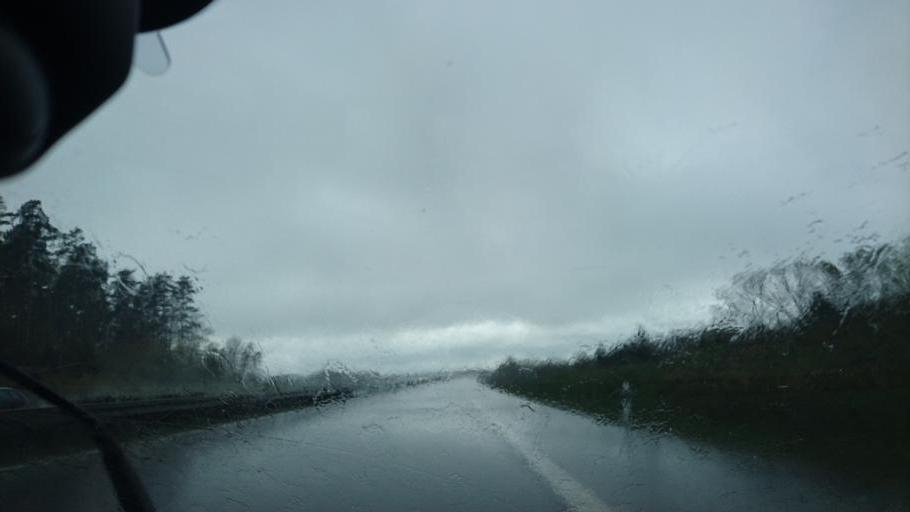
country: DE
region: Mecklenburg-Vorpommern
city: Tessin
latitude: 54.0108
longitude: 12.4610
